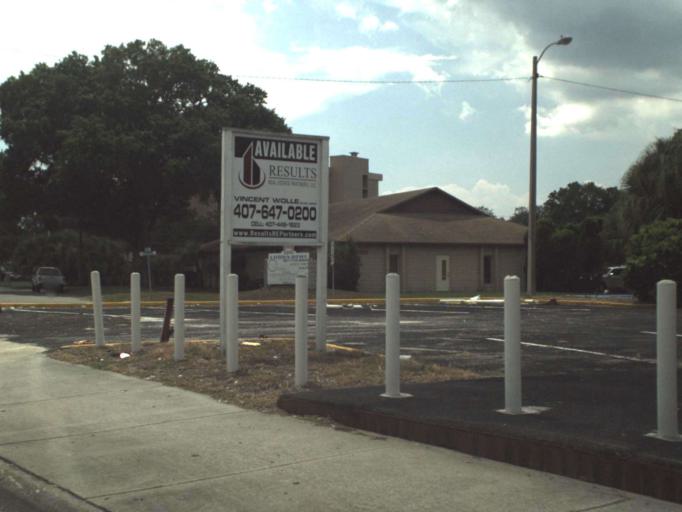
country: US
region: Florida
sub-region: Orange County
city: Fairview Shores
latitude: 28.6058
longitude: -81.4035
